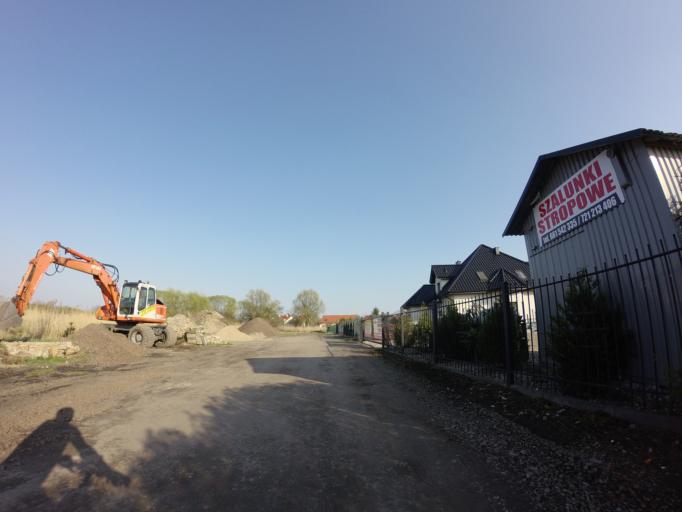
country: PL
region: West Pomeranian Voivodeship
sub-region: Powiat choszczenski
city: Choszczno
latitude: 53.1703
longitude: 15.4325
